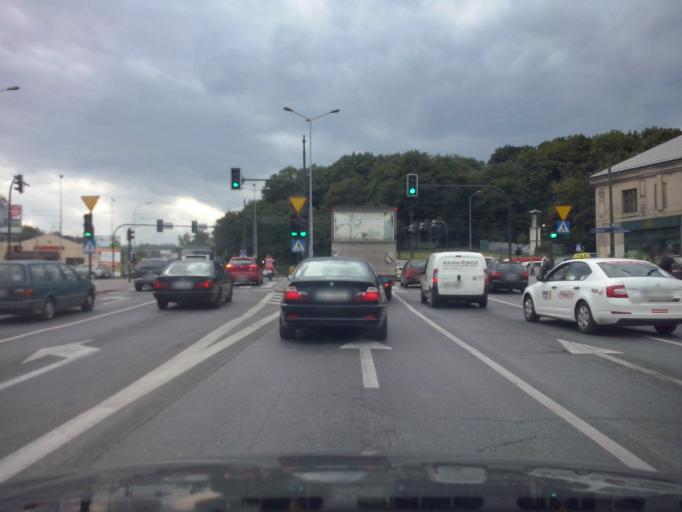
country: PL
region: Lesser Poland Voivodeship
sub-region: Krakow
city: Krakow
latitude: 50.0423
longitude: 19.9619
